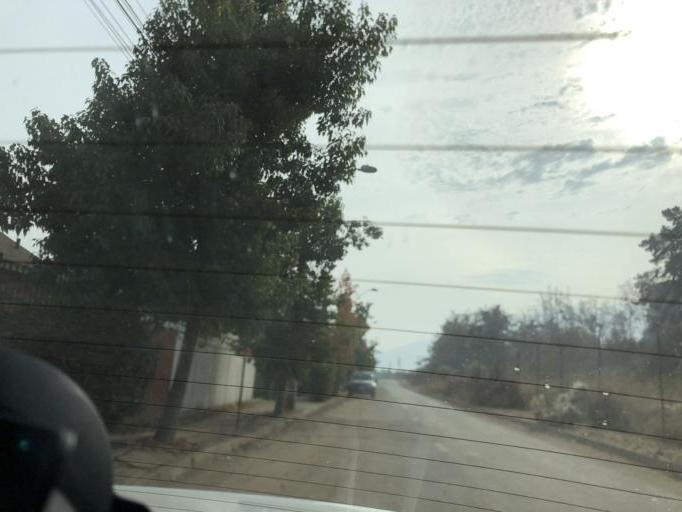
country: CL
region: Santiago Metropolitan
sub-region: Provincia de Cordillera
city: Puente Alto
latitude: -33.5672
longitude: -70.5441
